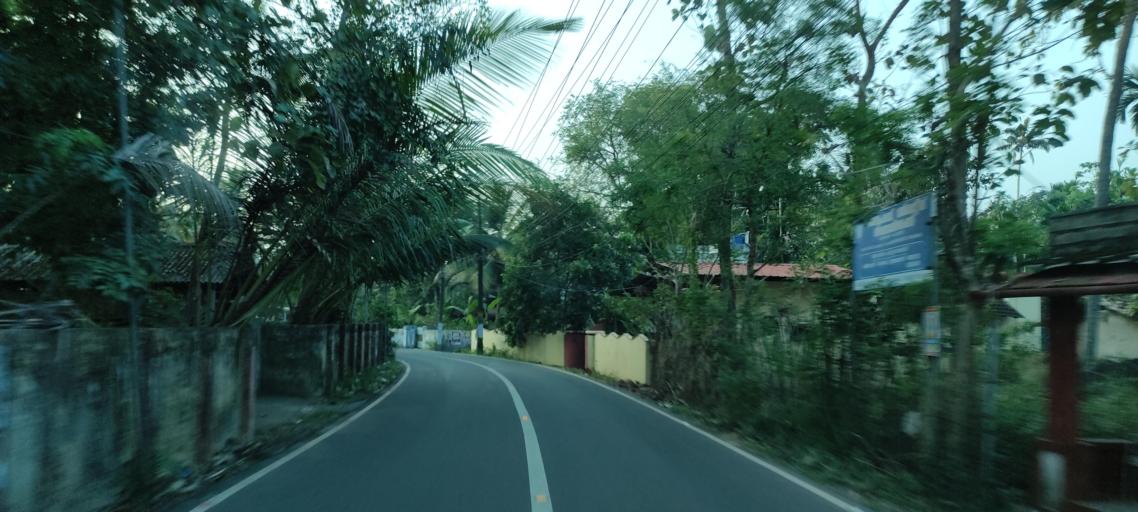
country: IN
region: Kerala
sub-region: Alappuzha
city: Alleppey
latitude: 9.4455
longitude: 76.3459
